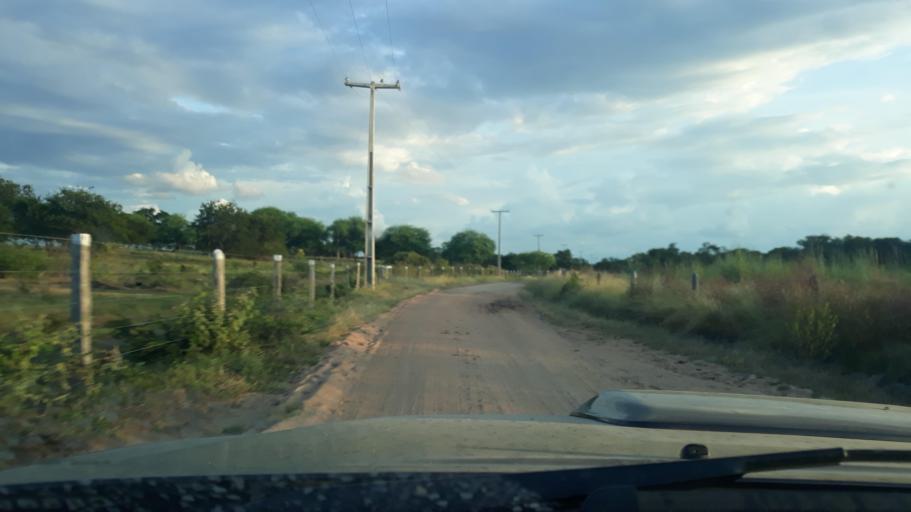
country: BR
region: Bahia
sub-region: Riacho De Santana
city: Riacho de Santana
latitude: -13.8782
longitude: -43.0207
